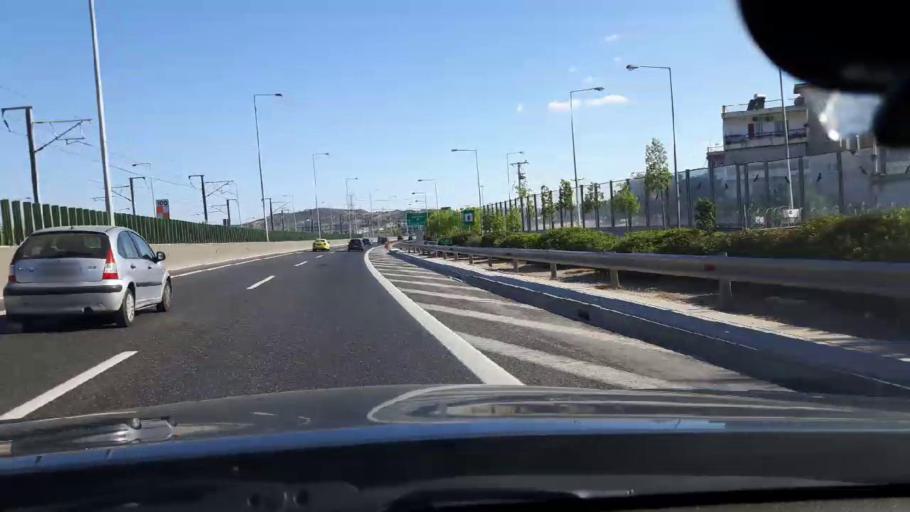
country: GR
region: Attica
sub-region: Nomarchia Anatolikis Attikis
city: Leondarion
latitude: 37.9825
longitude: 23.8695
